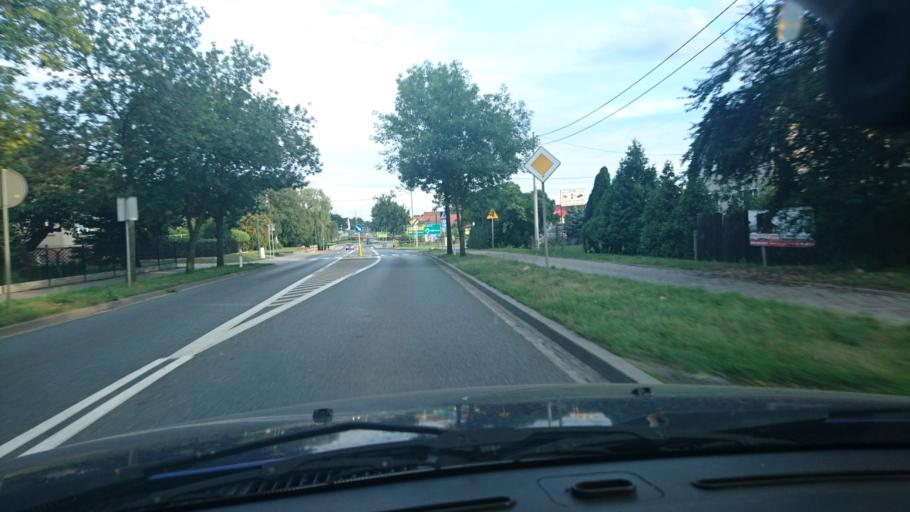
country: PL
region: Opole Voivodeship
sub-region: Powiat oleski
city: Olesno
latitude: 50.8769
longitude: 18.4127
